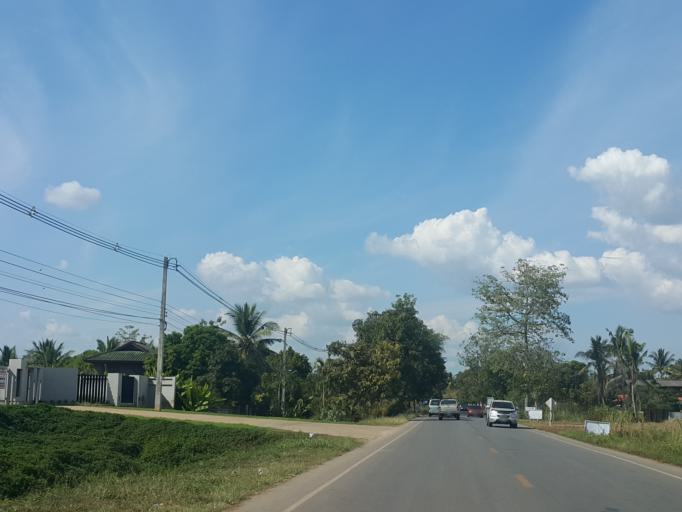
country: TH
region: Sukhothai
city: Sawankhalok
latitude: 17.2889
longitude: 99.8332
